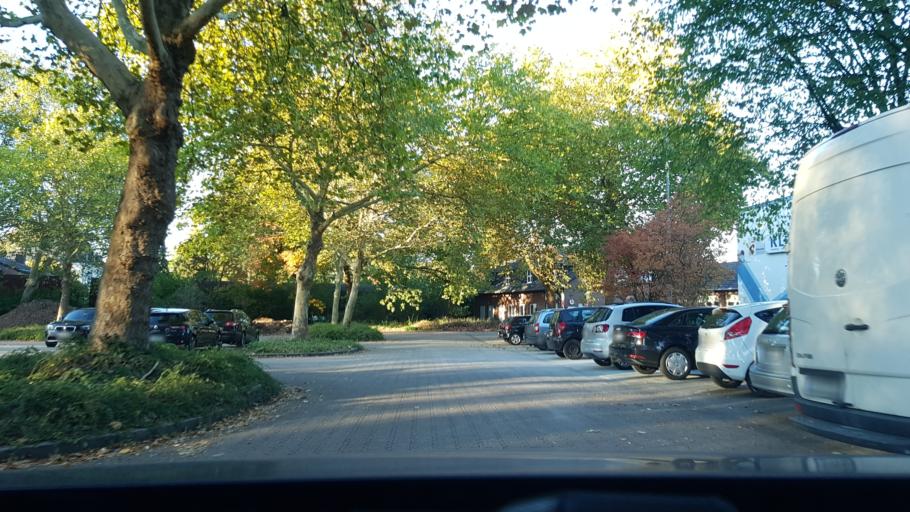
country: DE
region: North Rhine-Westphalia
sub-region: Regierungsbezirk Dusseldorf
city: Moers
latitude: 51.4442
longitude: 6.5789
